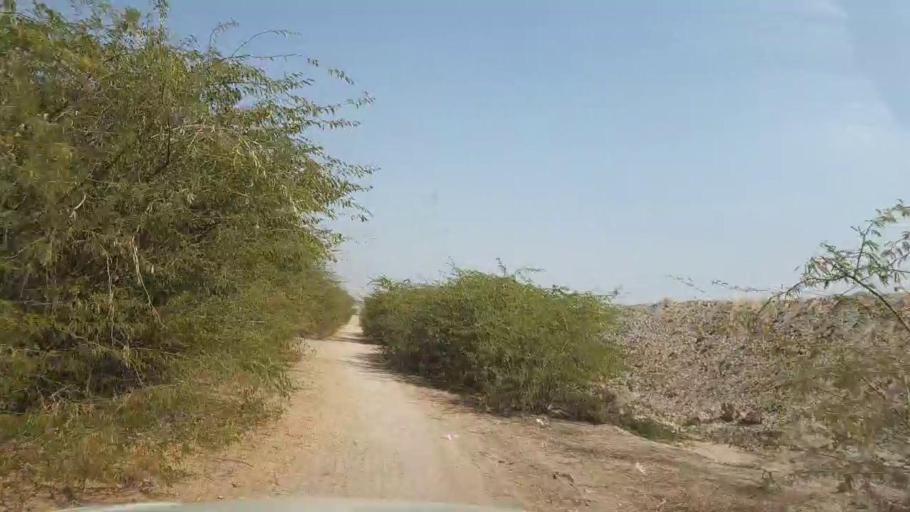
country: PK
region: Sindh
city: Nabisar
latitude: 25.0583
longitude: 69.5562
